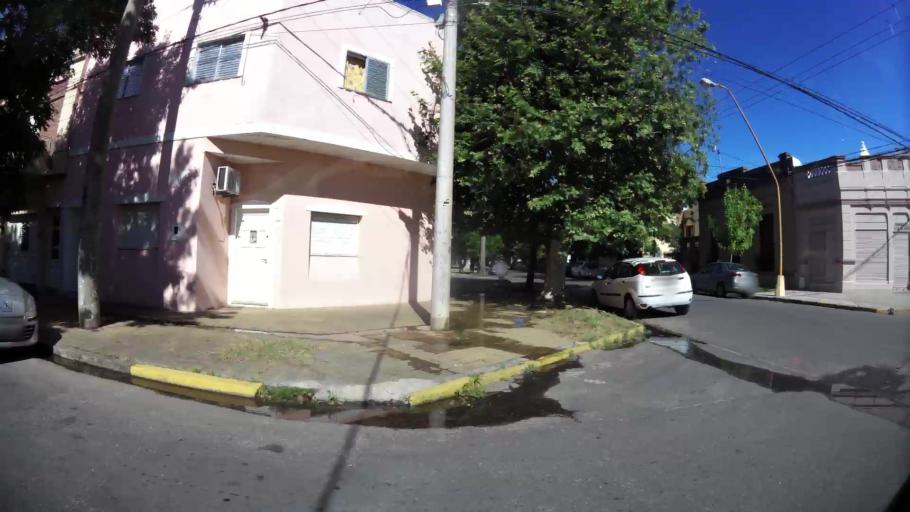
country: AR
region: Santa Fe
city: Santa Fe de la Vera Cruz
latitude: -31.6354
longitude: -60.6903
